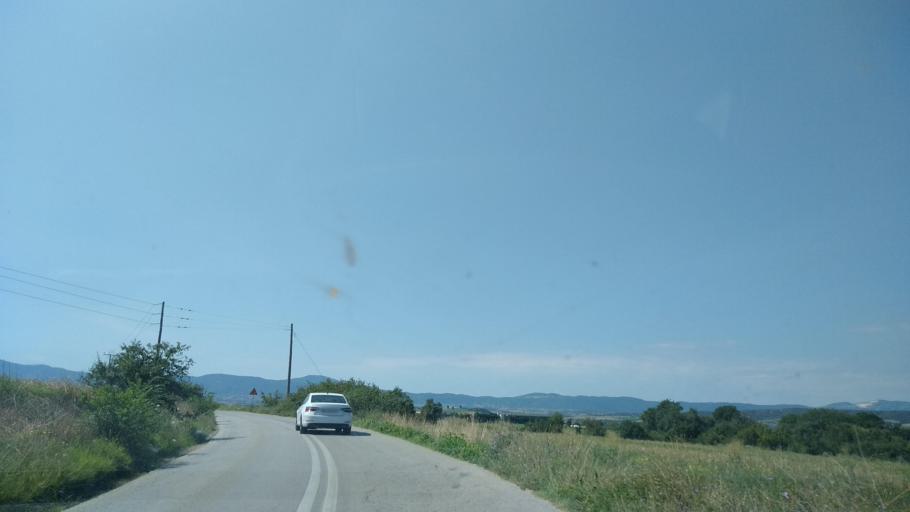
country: GR
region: Central Macedonia
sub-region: Nomos Thessalonikis
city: Nea Apollonia
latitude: 40.6086
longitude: 23.4567
